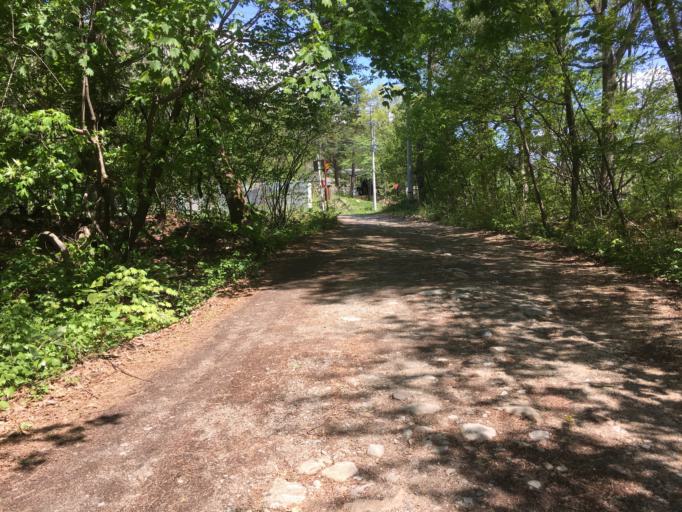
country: JP
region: Nagano
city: Omachi
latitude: 36.5137
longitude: 137.7940
